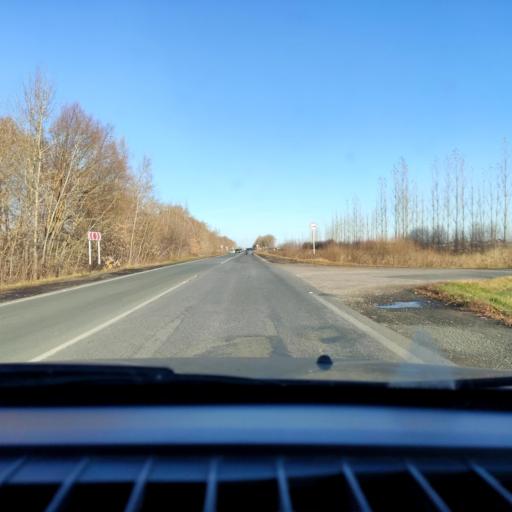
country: RU
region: Samara
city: Tol'yatti
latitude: 53.6184
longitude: 49.3110
